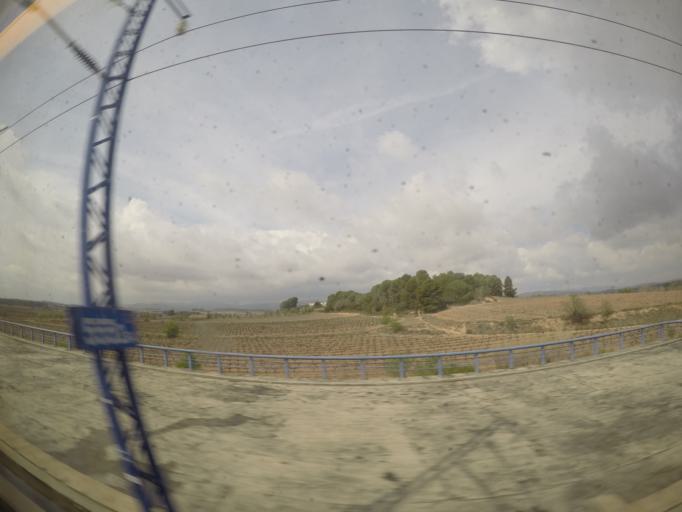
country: ES
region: Catalonia
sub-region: Provincia de Barcelona
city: Castellet
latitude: 41.2711
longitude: 1.5971
